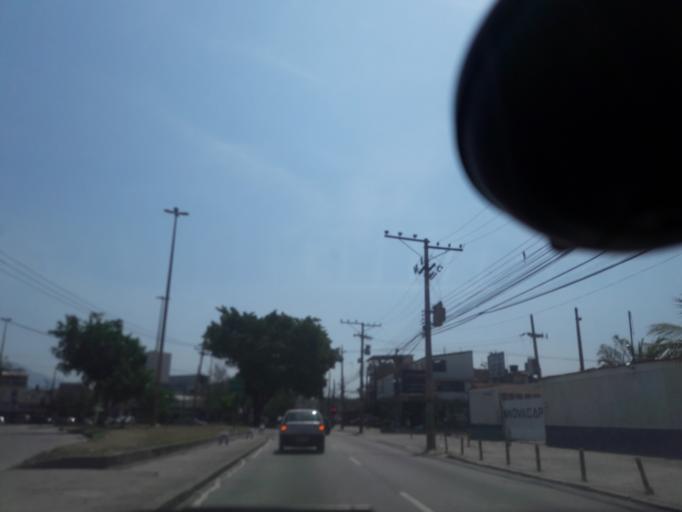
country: BR
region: Rio de Janeiro
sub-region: Sao Joao De Meriti
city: Sao Joao de Meriti
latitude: -22.8771
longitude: -43.3686
